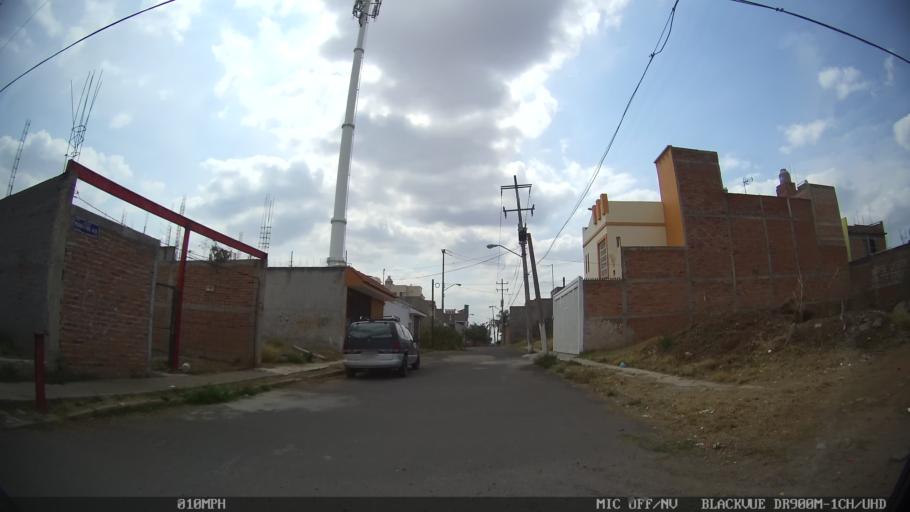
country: MX
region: Jalisco
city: Coyula
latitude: 20.6391
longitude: -103.2180
